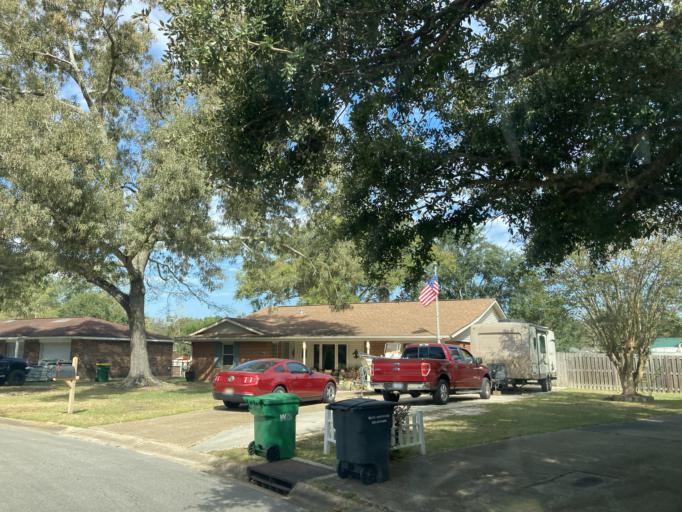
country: US
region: Mississippi
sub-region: Jackson County
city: Saint Martin
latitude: 30.4495
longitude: -88.8771
